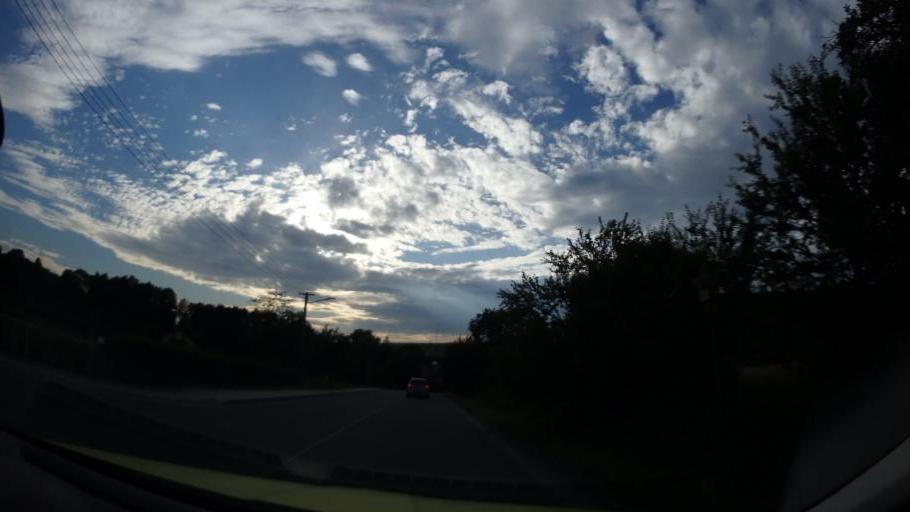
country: CZ
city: Rybi
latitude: 49.5995
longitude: 18.0830
